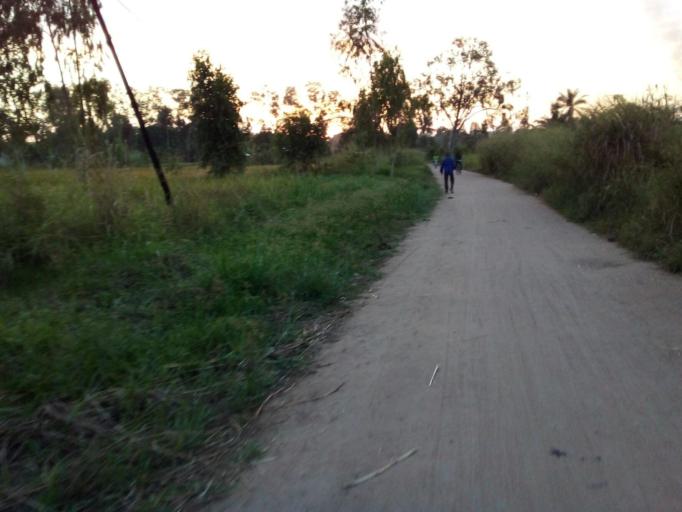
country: MZ
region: Zambezia
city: Quelimane
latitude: -17.6055
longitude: 36.8180
